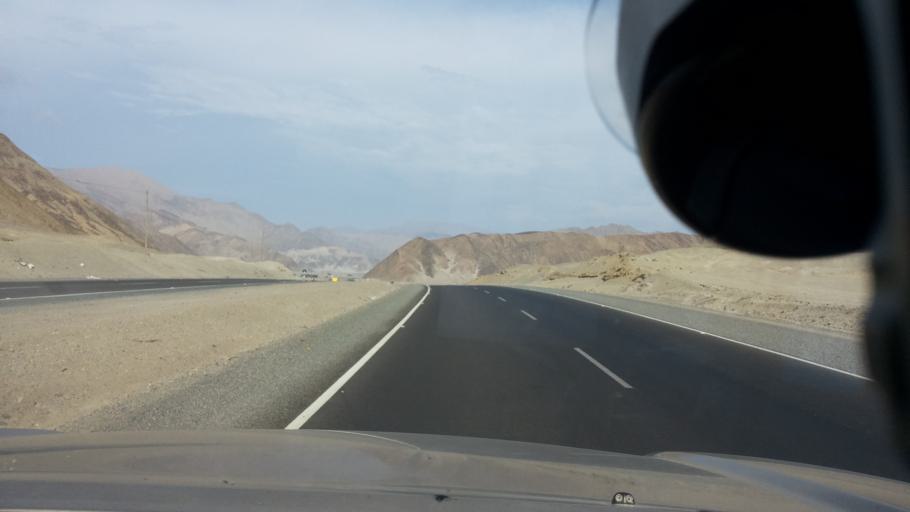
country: PE
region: Ancash
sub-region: Provincia de Huarmey
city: La Caleta Culebras
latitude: -9.7981
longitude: -78.2000
